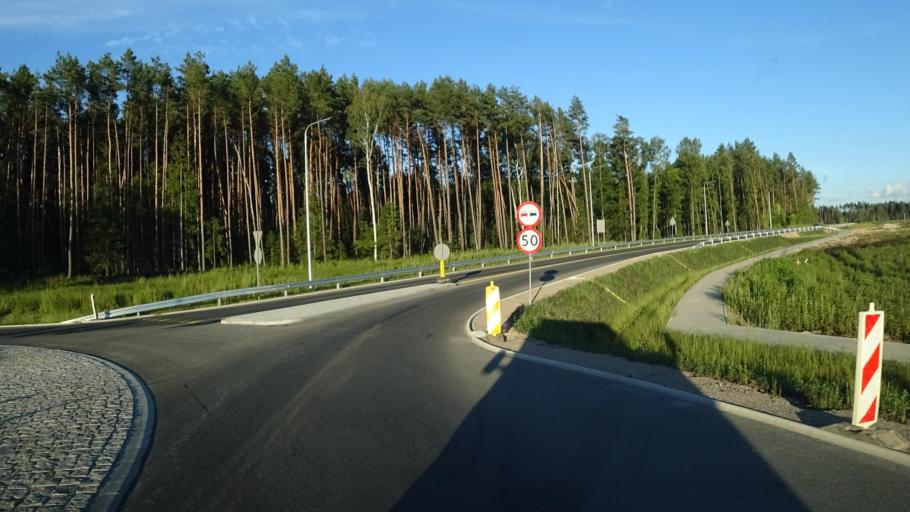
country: PL
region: Warmian-Masurian Voivodeship
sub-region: Powiat elcki
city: Elk
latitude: 53.8402
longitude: 22.4183
